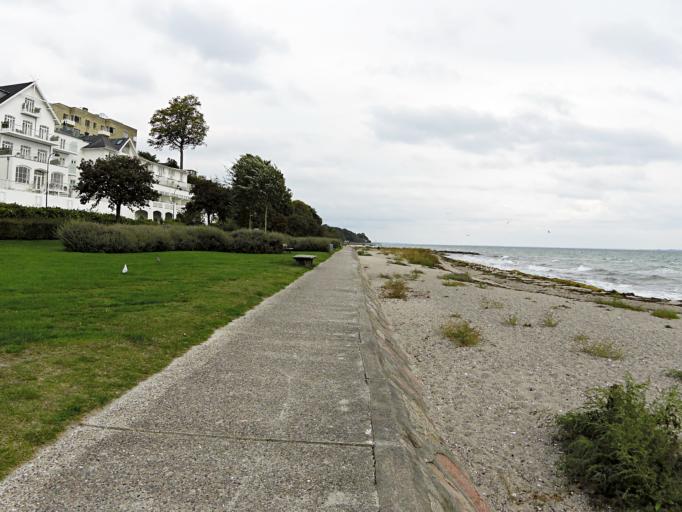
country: DK
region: Capital Region
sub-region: Rudersdal Kommune
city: Trorod
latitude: 55.8279
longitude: 12.5747
